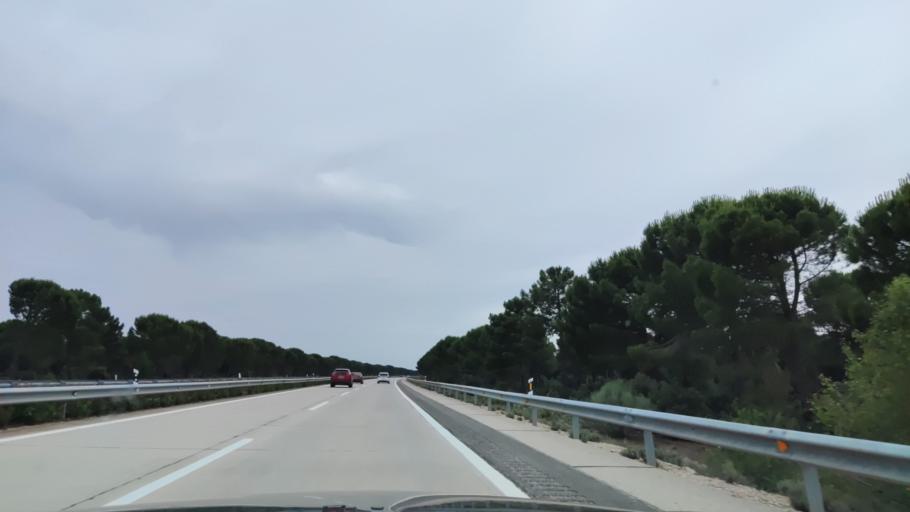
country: ES
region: Castille-La Mancha
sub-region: Provincia de Cuenca
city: Pozoamargo
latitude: 39.3428
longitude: -2.1996
